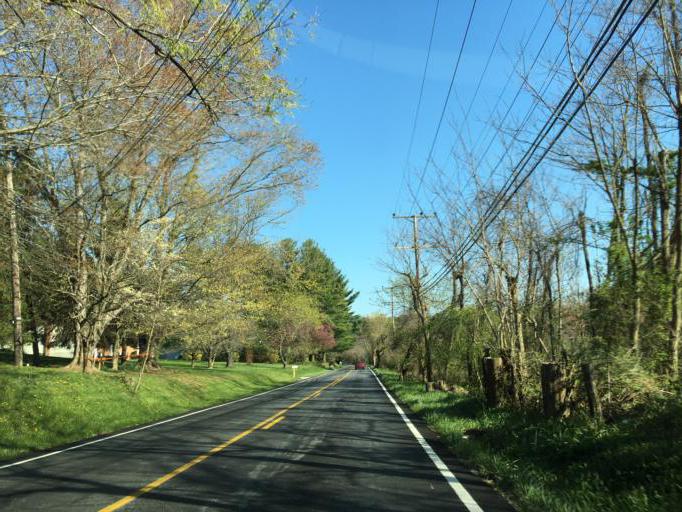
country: US
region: Maryland
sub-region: Baltimore County
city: Hampton
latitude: 39.5044
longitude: -76.5341
